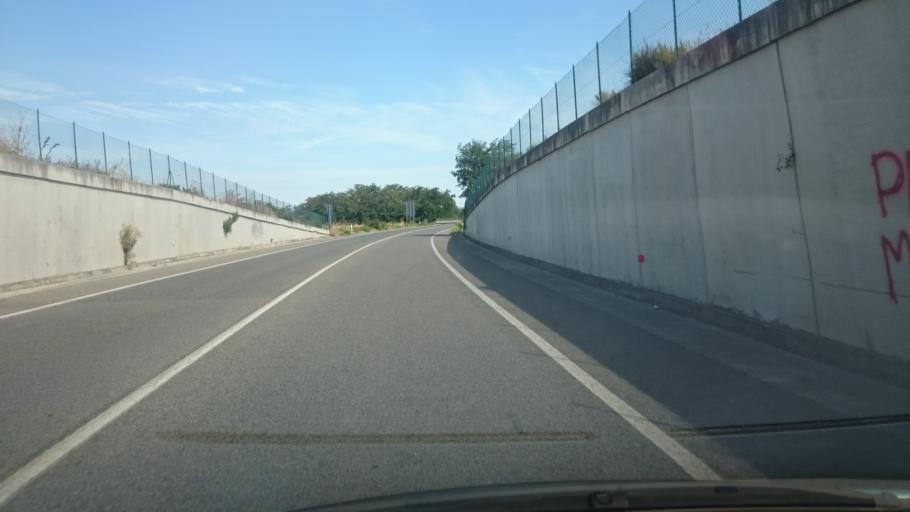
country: IT
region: Emilia-Romagna
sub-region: Provincia di Reggio Emilia
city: Casalgrande
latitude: 44.5825
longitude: 10.7366
